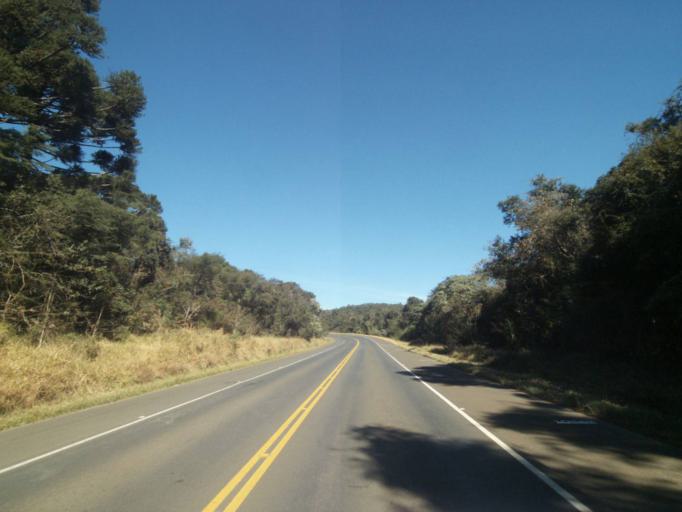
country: BR
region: Parana
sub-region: Tibagi
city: Tibagi
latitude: -24.5509
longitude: -50.4550
